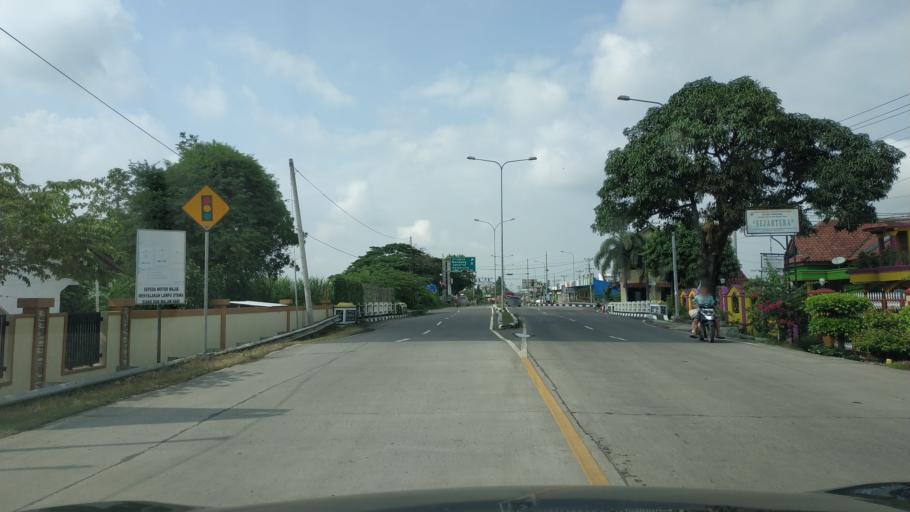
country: ID
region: Central Java
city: Ketanggungan
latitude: -6.8935
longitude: 108.8859
